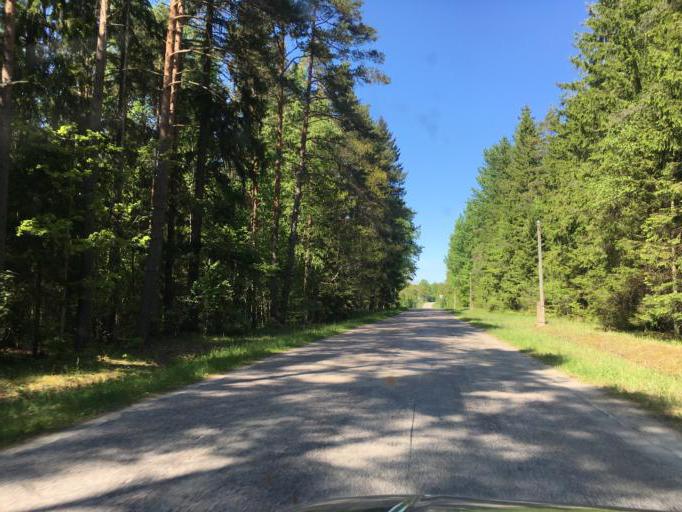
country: LV
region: Dundaga
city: Dundaga
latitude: 57.4884
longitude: 22.3420
